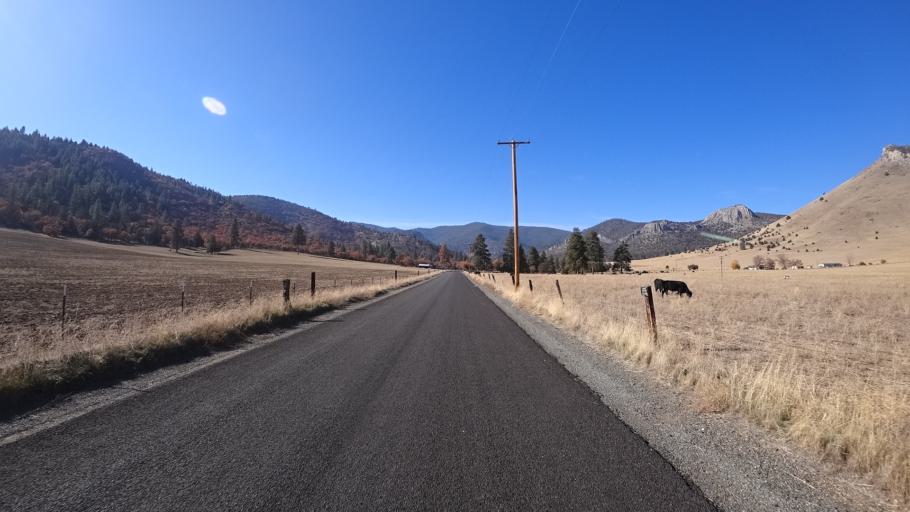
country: US
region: California
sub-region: Siskiyou County
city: Weed
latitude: 41.5028
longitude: -122.5654
